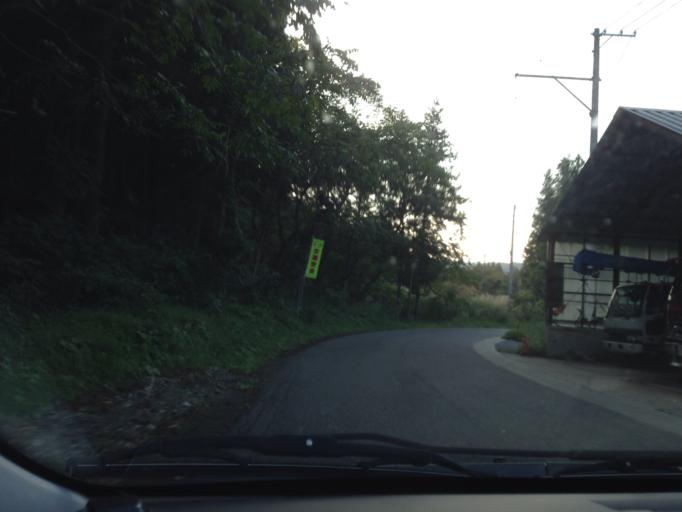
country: JP
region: Fukushima
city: Kitakata
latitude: 37.4863
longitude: 139.6844
